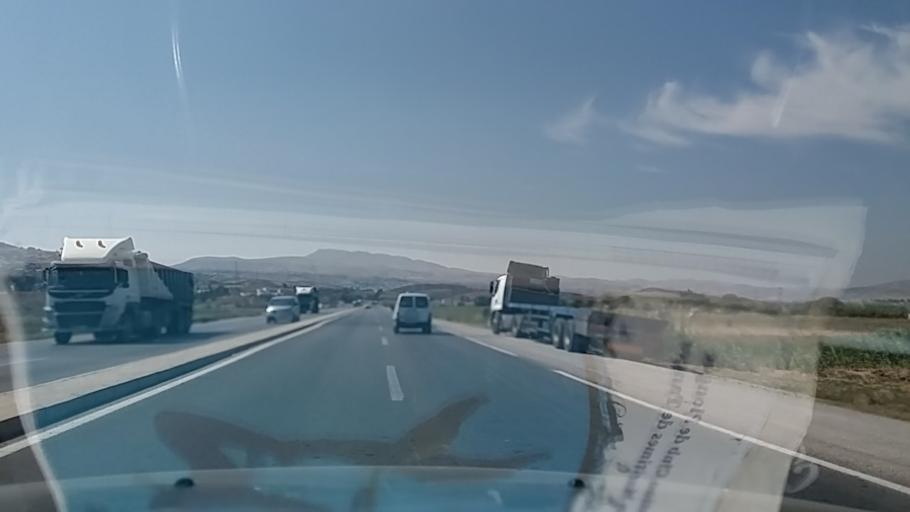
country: MA
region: Tanger-Tetouan
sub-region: Tetouan
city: Saddina
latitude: 35.5589
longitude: -5.4591
